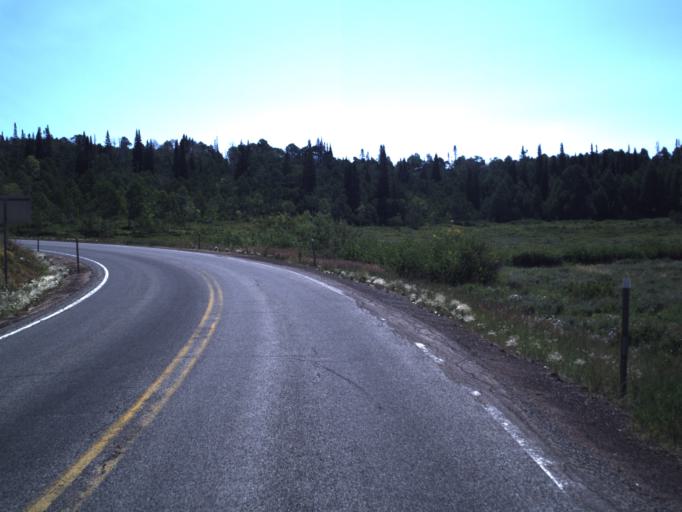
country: US
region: Utah
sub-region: Sanpete County
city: Fairview
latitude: 39.6763
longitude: -111.3222
